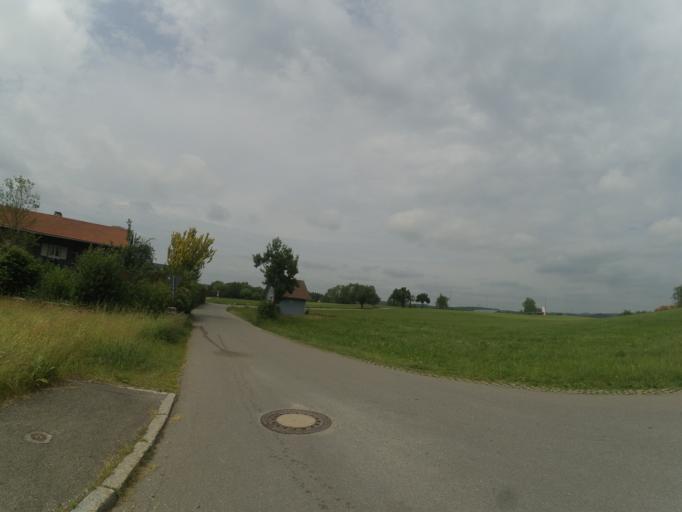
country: DE
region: Baden-Wuerttemberg
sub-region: Tuebingen Region
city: Isny im Allgau
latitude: 47.7444
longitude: 10.0130
